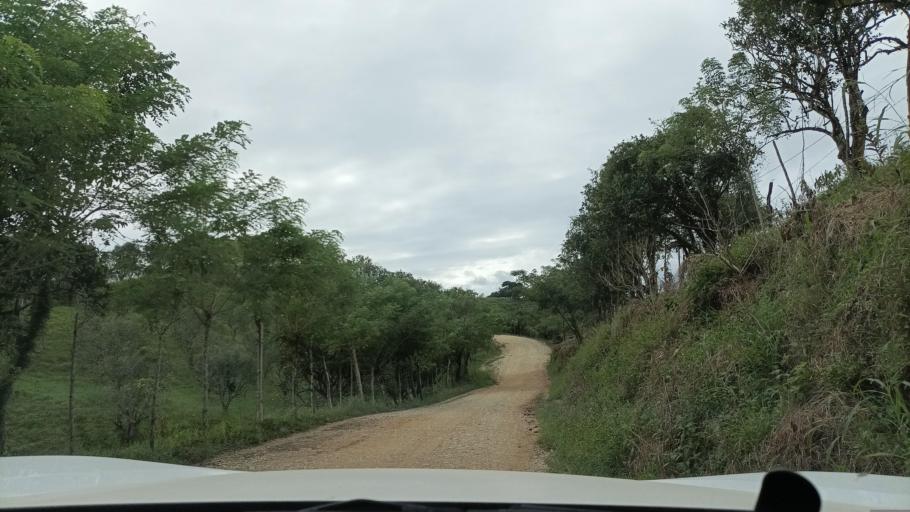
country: MX
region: Veracruz
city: Hidalgotitlan
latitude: 17.6035
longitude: -94.4268
